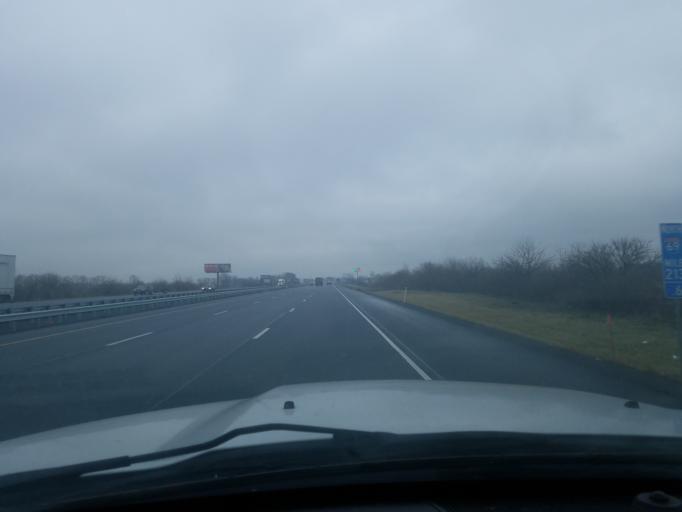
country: US
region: Indiana
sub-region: Hancock County
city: Fortville
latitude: 39.9923
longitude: -85.8593
